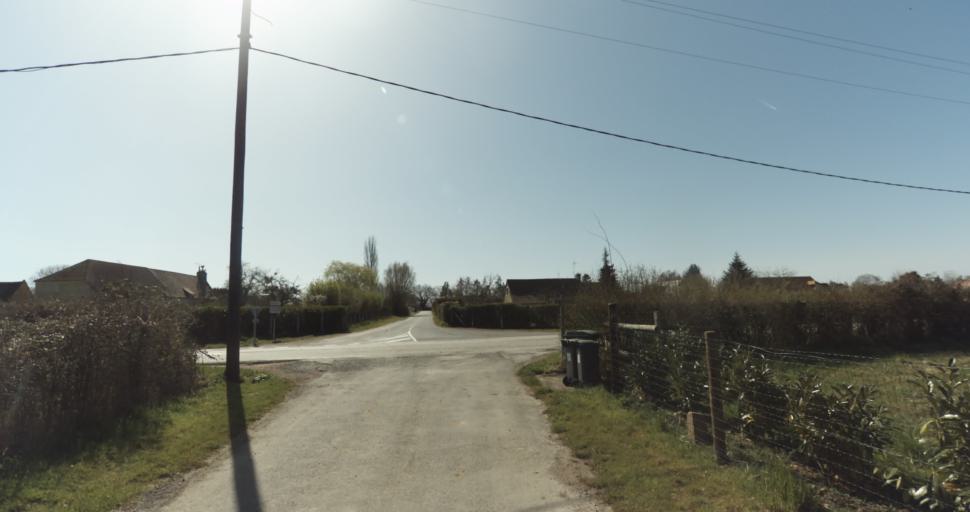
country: FR
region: Lower Normandy
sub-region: Departement du Calvados
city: Saint-Pierre-sur-Dives
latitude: 49.0194
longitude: -0.0047
